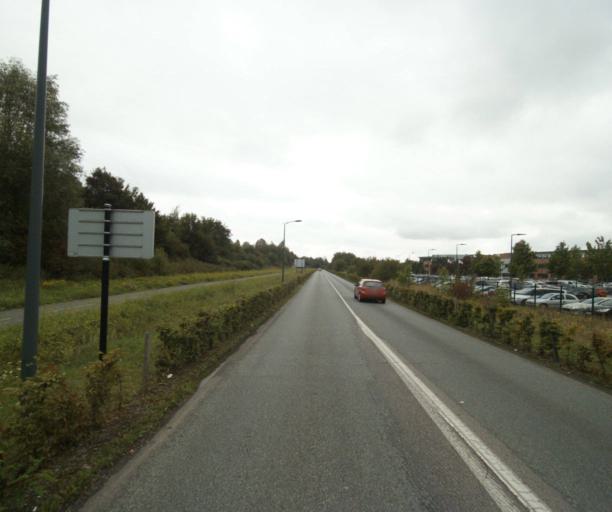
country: FR
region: Nord-Pas-de-Calais
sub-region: Departement du Nord
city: Lezennes
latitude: 50.6113
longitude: 3.1218
